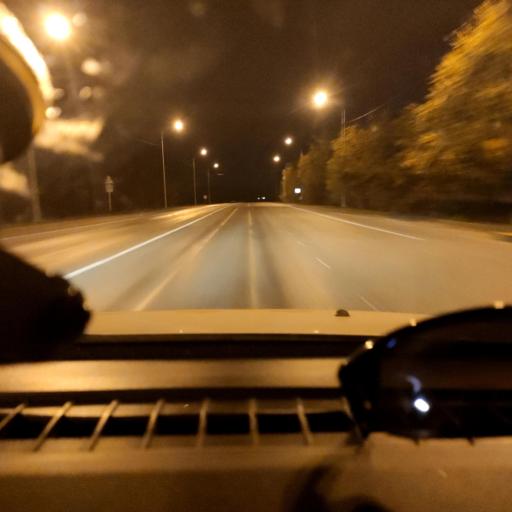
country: RU
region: Samara
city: Samara
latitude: 53.0808
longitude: 50.0893
